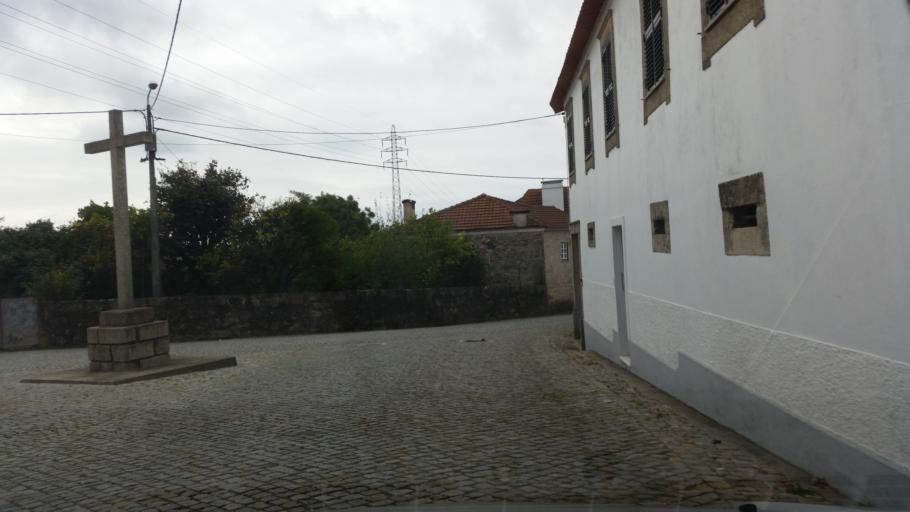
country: PT
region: Porto
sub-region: Valongo
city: Ermesinde
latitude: 41.2441
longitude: -8.5492
